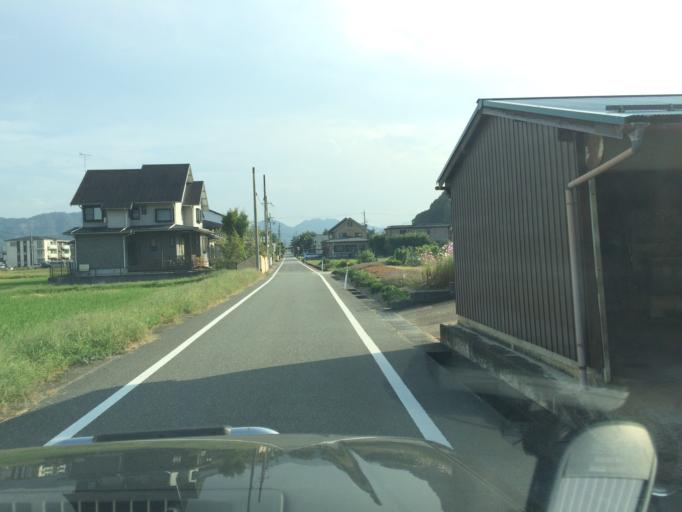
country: JP
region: Hyogo
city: Toyooka
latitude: 35.4799
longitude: 134.7774
